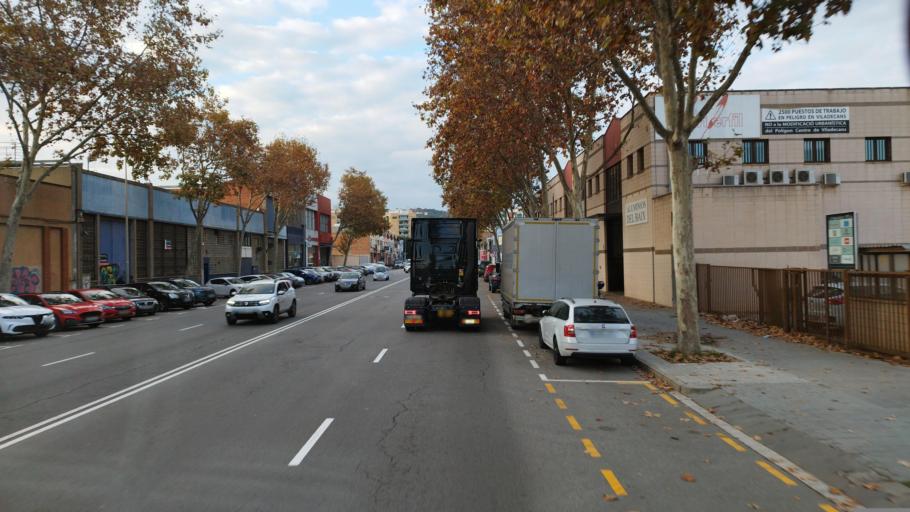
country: ES
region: Catalonia
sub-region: Provincia de Barcelona
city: Viladecans
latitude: 41.3093
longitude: 2.0190
